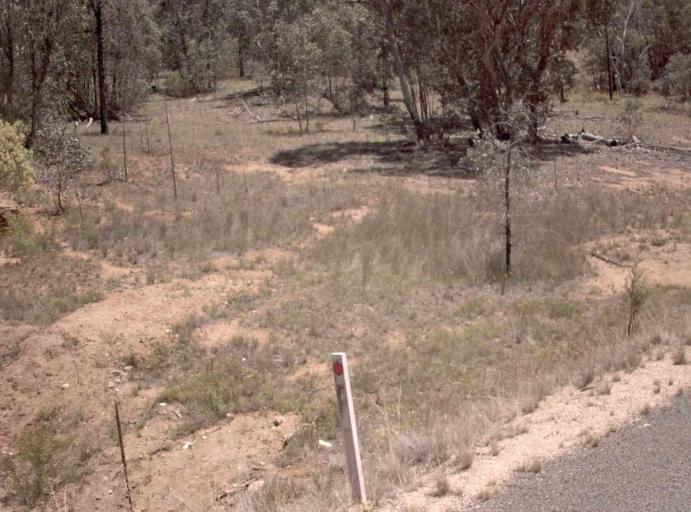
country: AU
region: New South Wales
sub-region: Snowy River
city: Jindabyne
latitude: -36.9249
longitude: 148.3895
